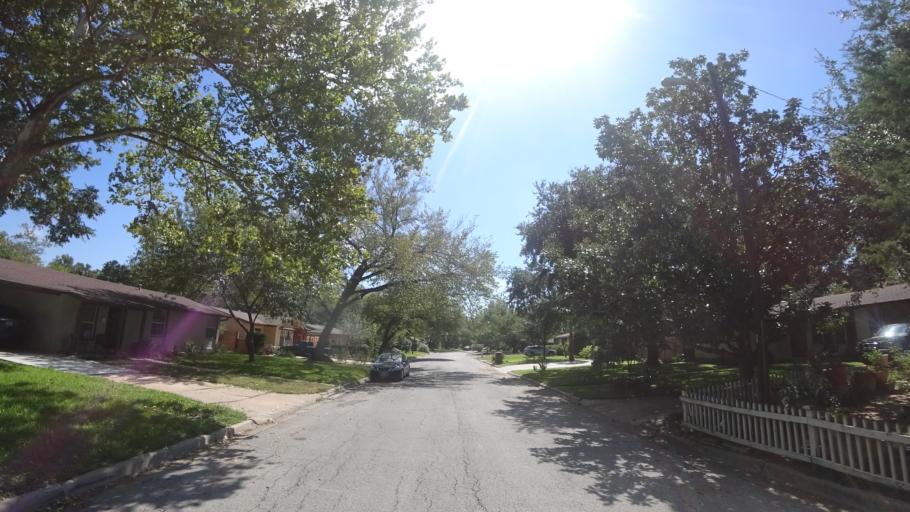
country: US
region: Texas
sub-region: Travis County
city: Austin
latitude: 30.3159
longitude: -97.6881
